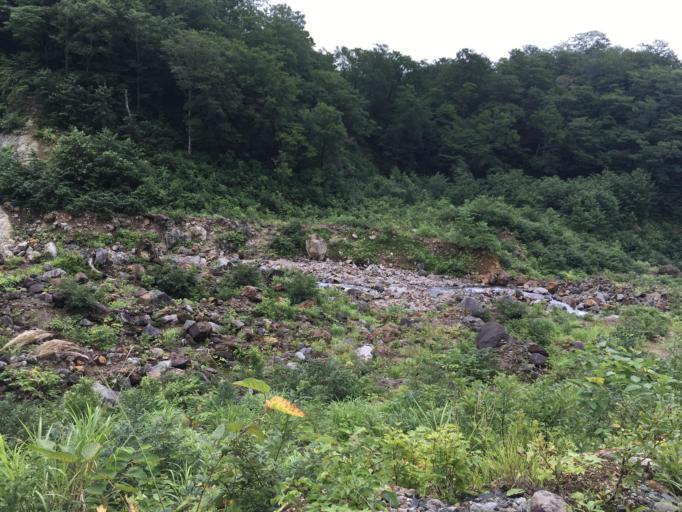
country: JP
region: Iwate
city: Ichinoseki
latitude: 38.9634
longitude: 140.8423
